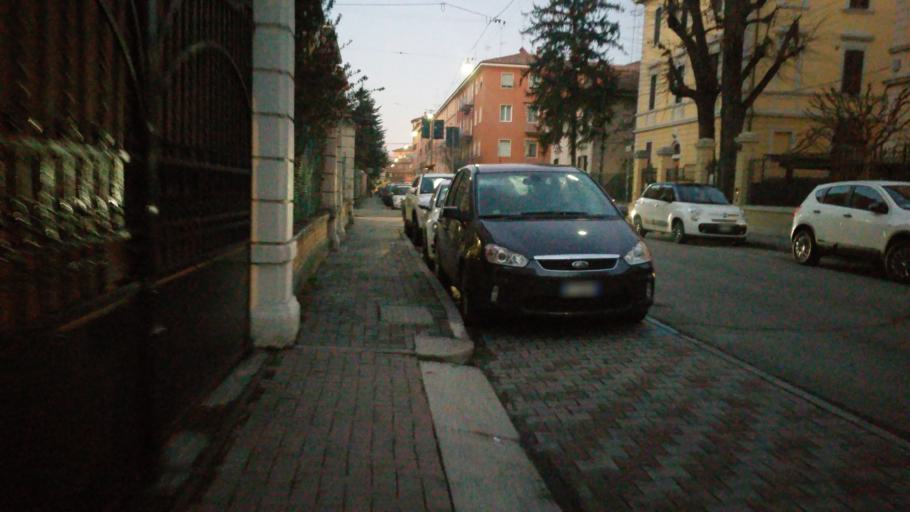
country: IT
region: Emilia-Romagna
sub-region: Provincia di Bologna
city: Bologna
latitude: 44.4988
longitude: 11.3216
